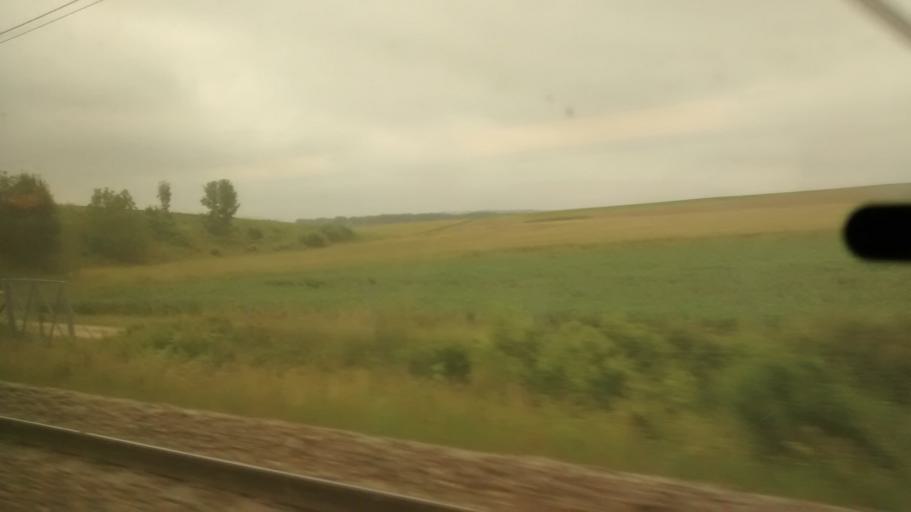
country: FR
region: Bourgogne
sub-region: Departement de l'Yonne
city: Brienon-sur-Armancon
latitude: 48.0098
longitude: 3.6375
